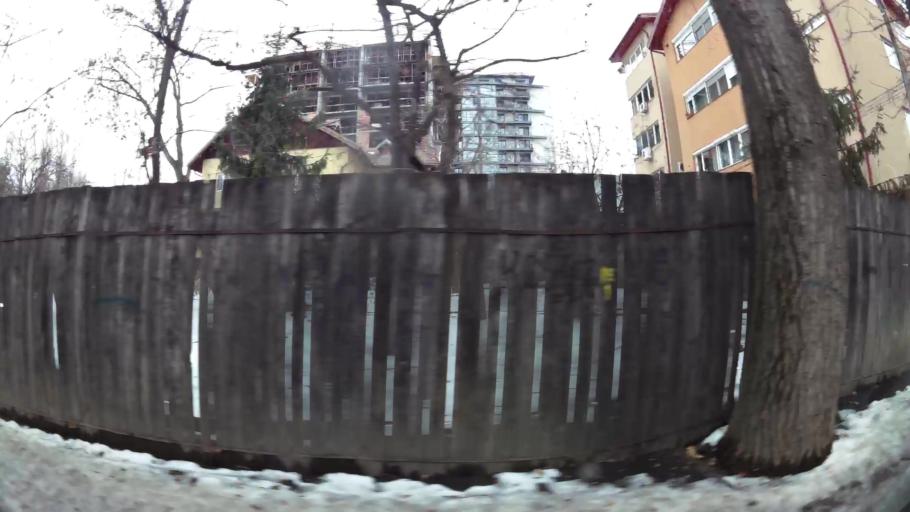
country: RO
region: Ilfov
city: Dobroesti
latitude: 44.4224
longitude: 26.1721
